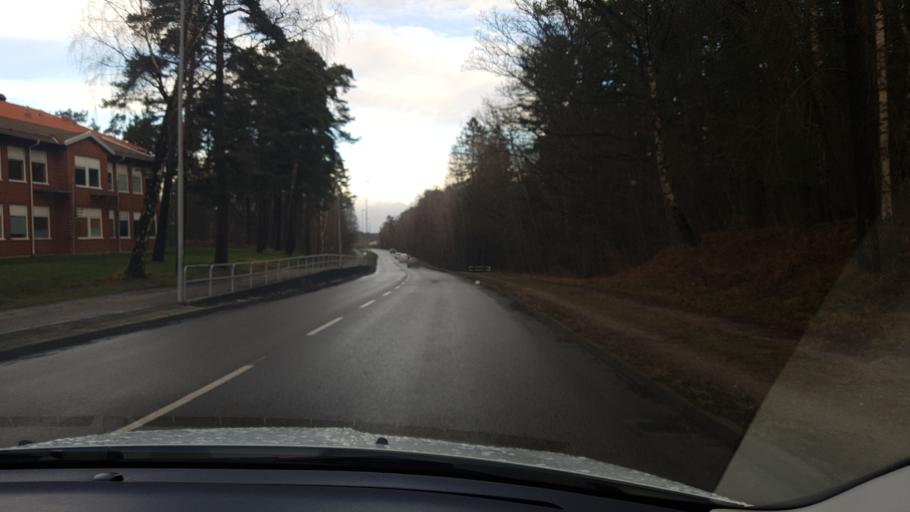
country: SE
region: Skane
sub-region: Hassleholms Kommun
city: Hassleholm
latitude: 56.1550
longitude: 13.7815
